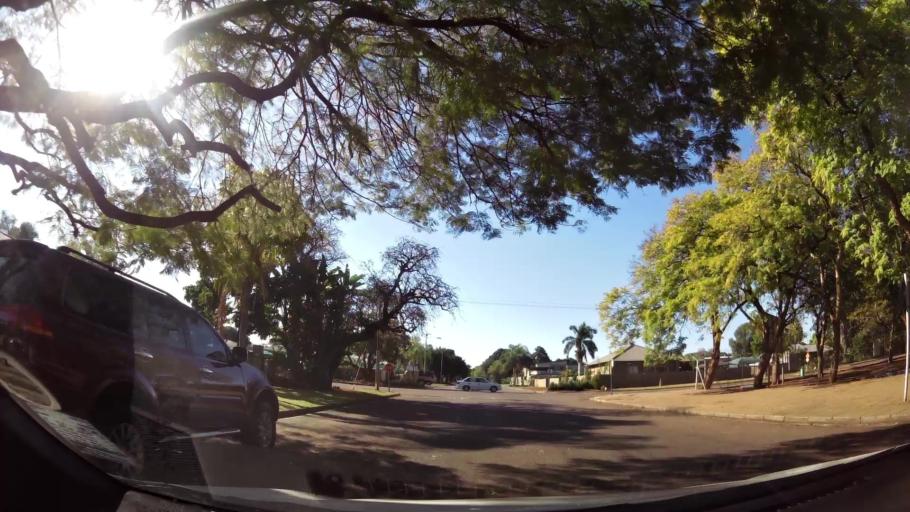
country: ZA
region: Limpopo
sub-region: Waterberg District Municipality
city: Mokopane
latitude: -24.1839
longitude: 29.0038
